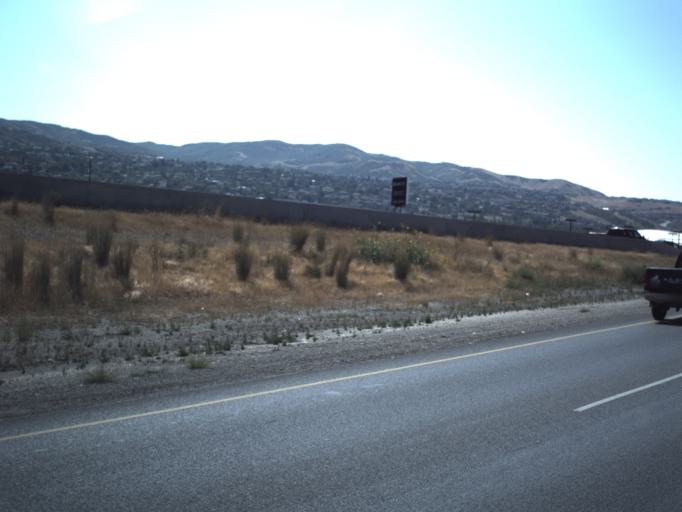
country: US
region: Utah
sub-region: Davis County
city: North Salt Lake
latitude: 40.8610
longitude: -111.9034
